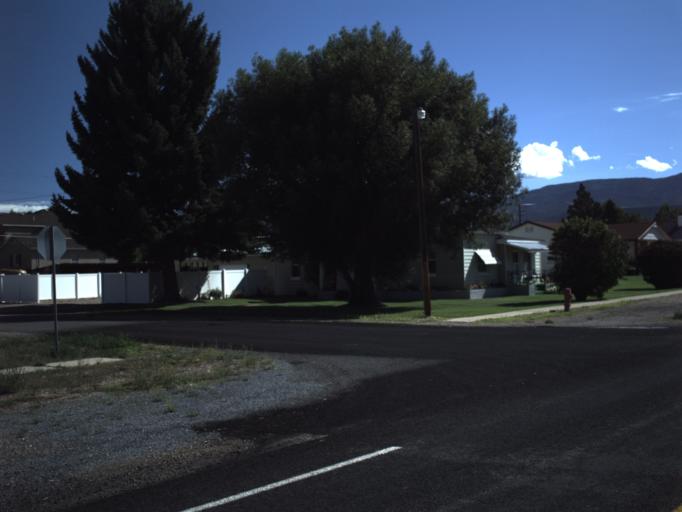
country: US
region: Utah
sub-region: Beaver County
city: Beaver
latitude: 38.2770
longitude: -112.6329
